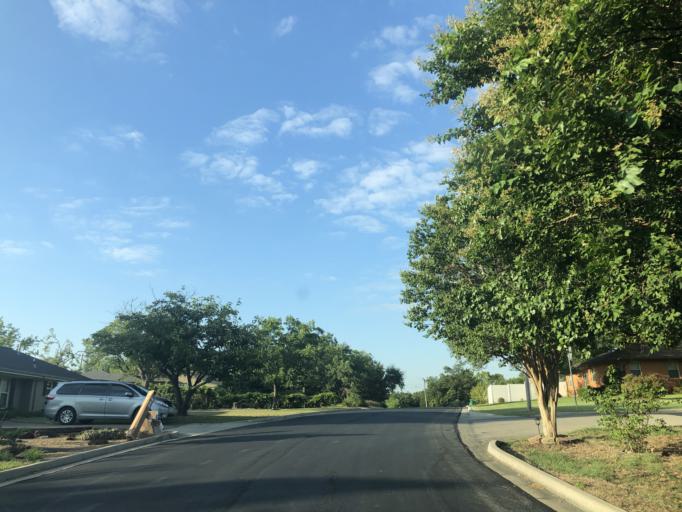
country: US
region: Texas
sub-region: Dallas County
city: Grand Prairie
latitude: 32.7532
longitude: -97.0088
